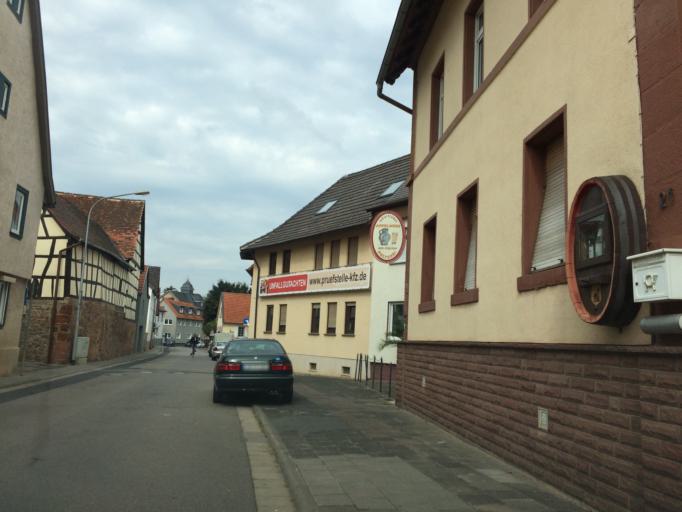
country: DE
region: Hesse
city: Gross-Umstadt
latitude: 49.8888
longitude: 8.9488
